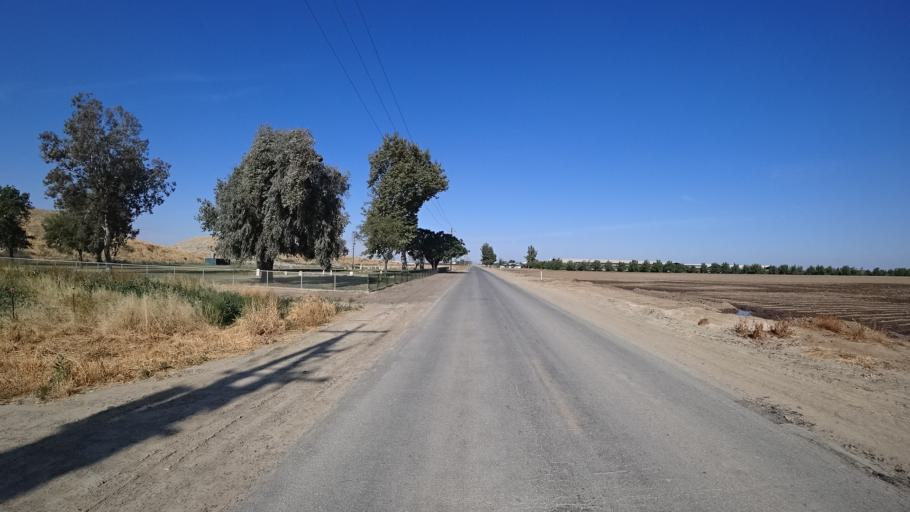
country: US
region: California
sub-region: Kings County
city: Home Garden
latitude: 36.2259
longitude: -119.6068
